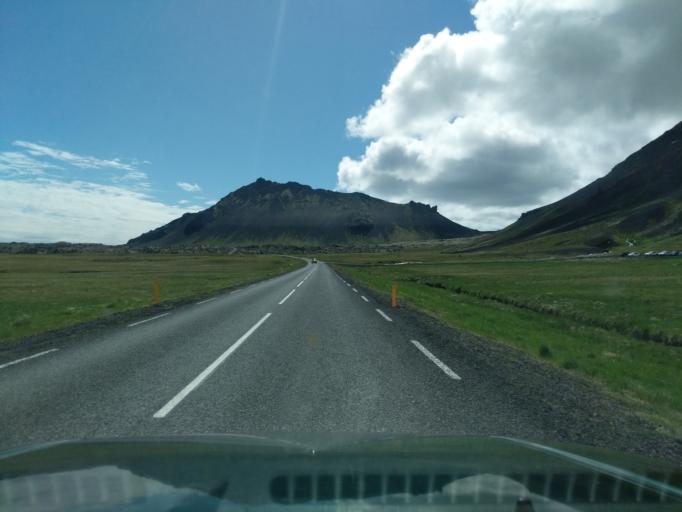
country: IS
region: West
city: Olafsvik
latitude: 64.7992
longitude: -23.6336
